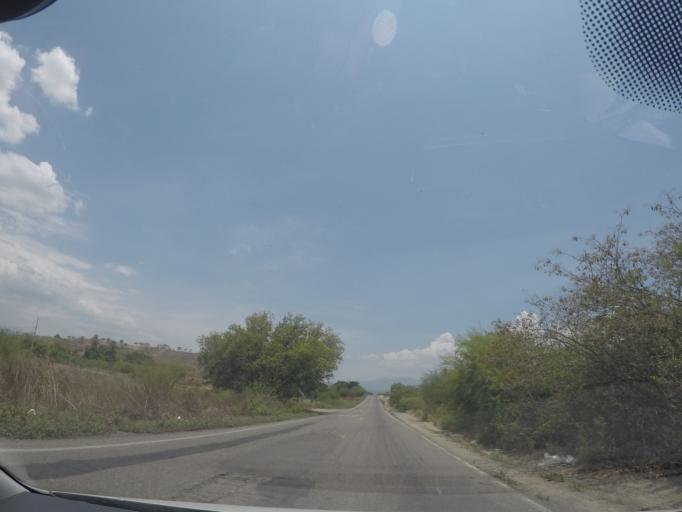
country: MX
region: Oaxaca
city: Santa Maria Jalapa del Marques
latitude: 16.4394
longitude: -95.5019
